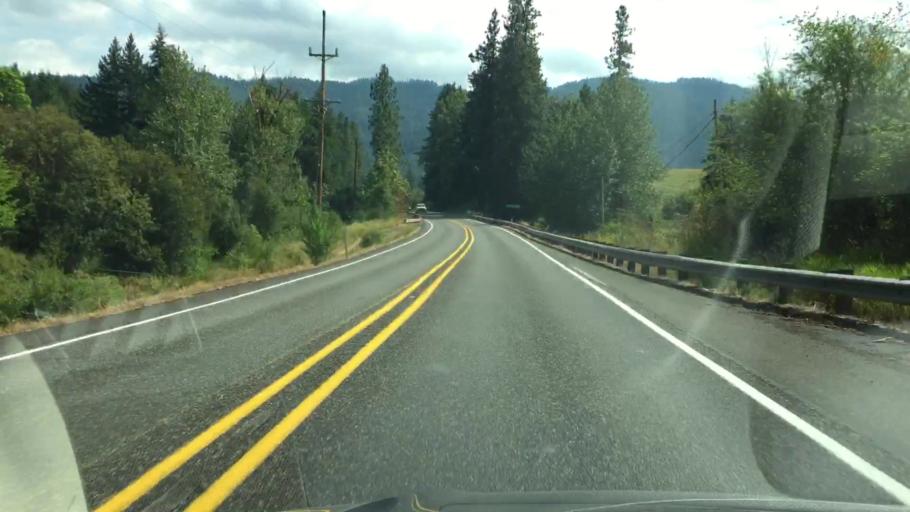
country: US
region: Washington
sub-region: Klickitat County
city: White Salmon
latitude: 45.8055
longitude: -121.4902
